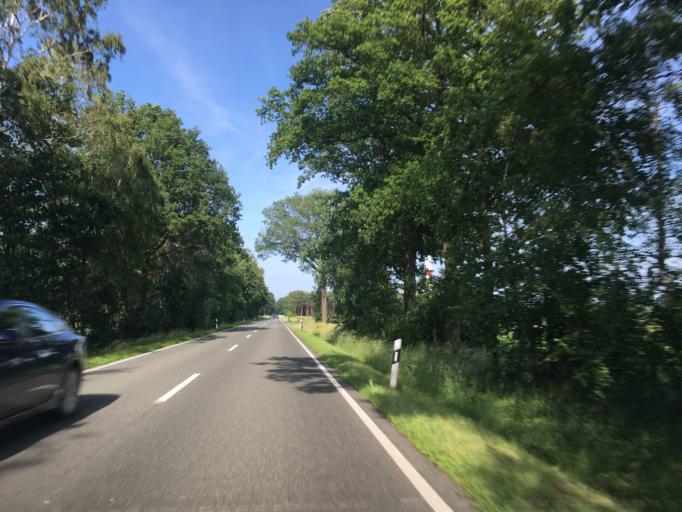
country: DE
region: North Rhine-Westphalia
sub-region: Regierungsbezirk Munster
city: Neuenkirchen
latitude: 52.1829
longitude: 7.4013
